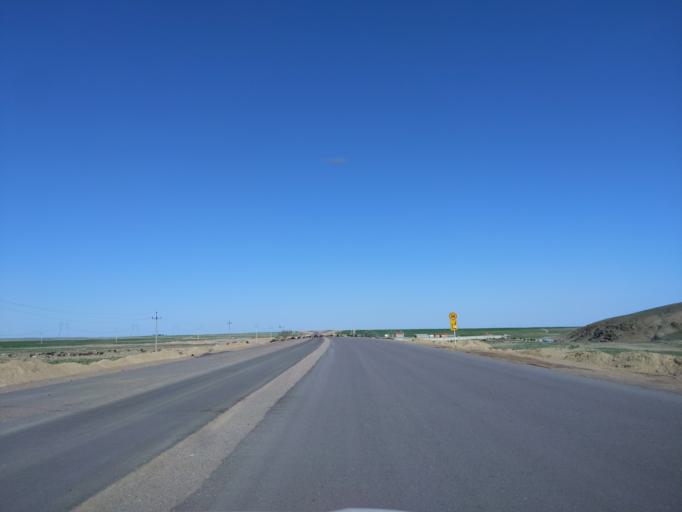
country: KZ
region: Almaty Oblysy
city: Bakanas
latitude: 44.0940
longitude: 75.9872
